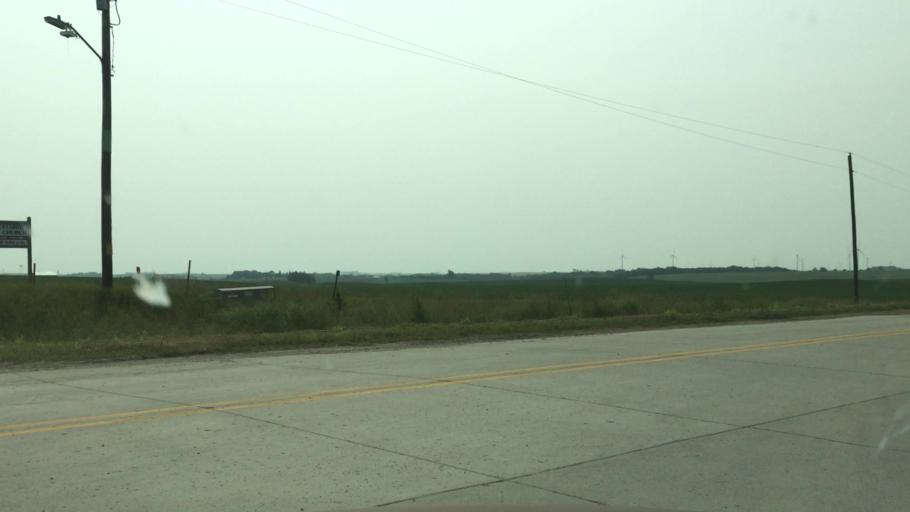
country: US
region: Iowa
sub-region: Dickinson County
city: Lake Park
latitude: 43.4303
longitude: -95.2891
